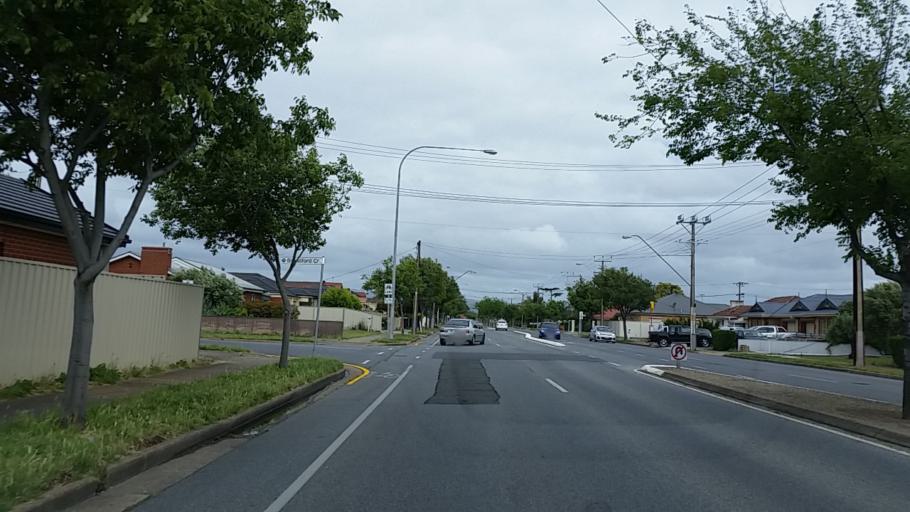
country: AU
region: South Australia
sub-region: Charles Sturt
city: Findon
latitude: -34.9004
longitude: 138.5399
